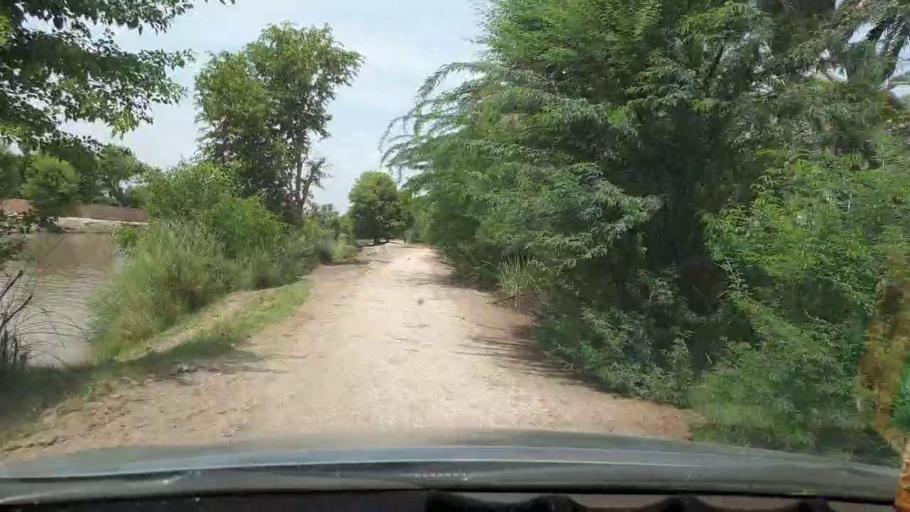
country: PK
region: Sindh
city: Khairpur
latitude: 27.4634
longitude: 68.8041
